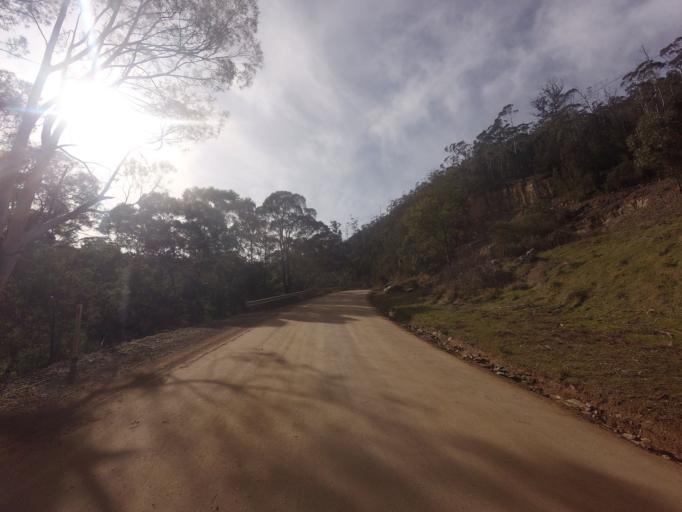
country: AU
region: Tasmania
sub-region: Huon Valley
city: Huonville
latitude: -43.0669
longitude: 147.0890
